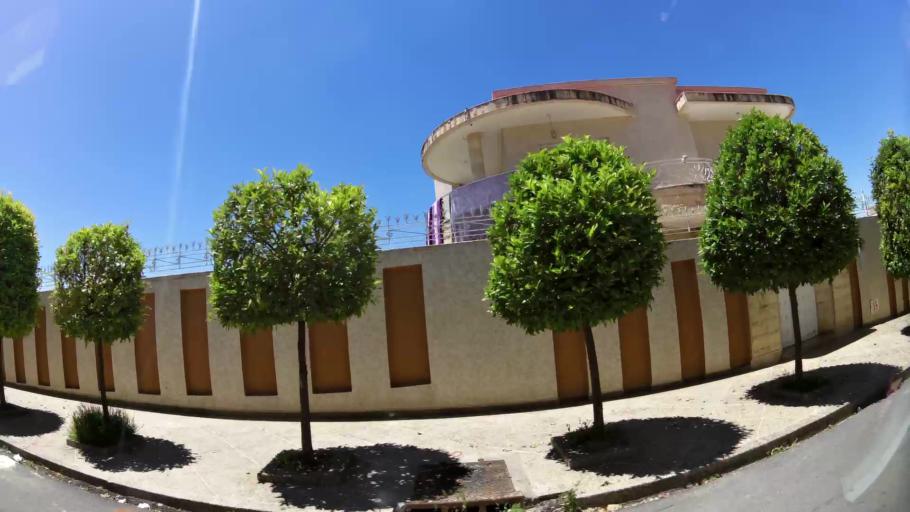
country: MA
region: Meknes-Tafilalet
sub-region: Meknes
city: Meknes
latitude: 33.9113
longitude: -5.5626
